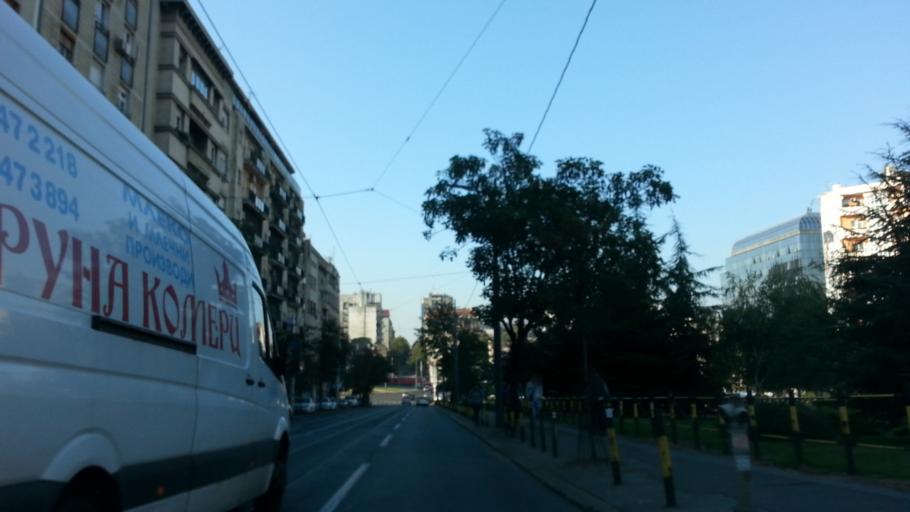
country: RS
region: Central Serbia
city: Belgrade
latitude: 44.8041
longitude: 20.4679
